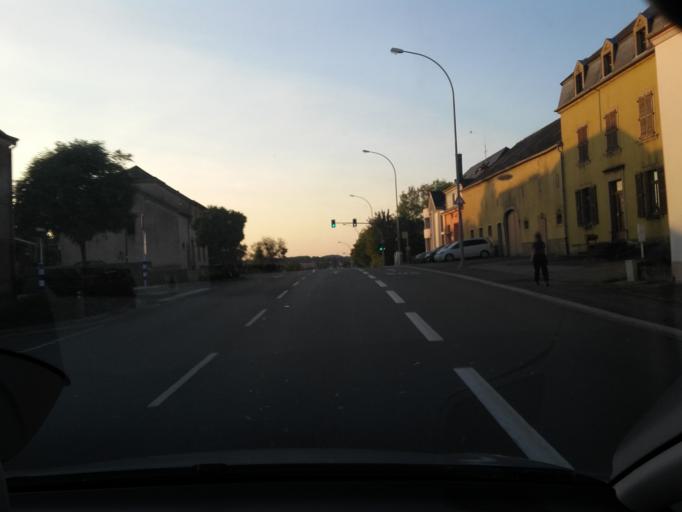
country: LU
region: Luxembourg
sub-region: Canton d'Esch-sur-Alzette
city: Frisange
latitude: 49.5138
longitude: 6.1893
